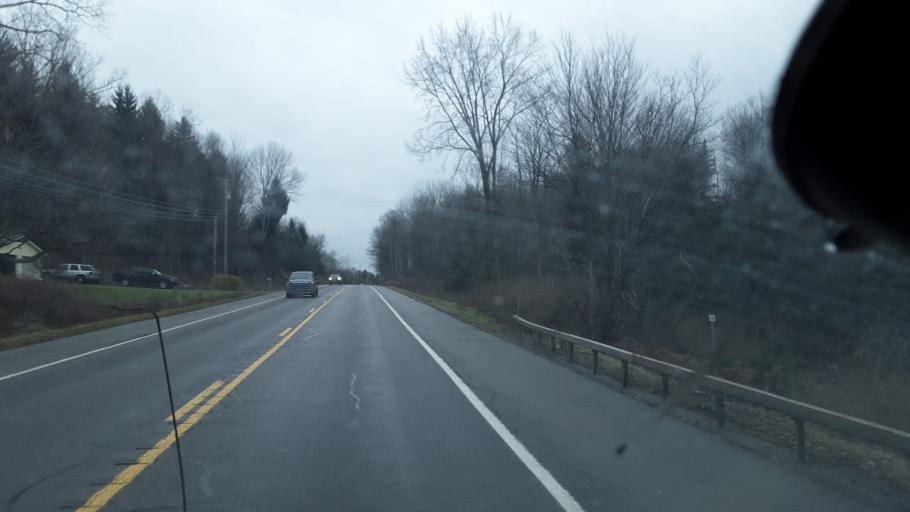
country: US
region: New York
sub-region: Erie County
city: Holland
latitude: 42.6063
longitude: -78.5018
